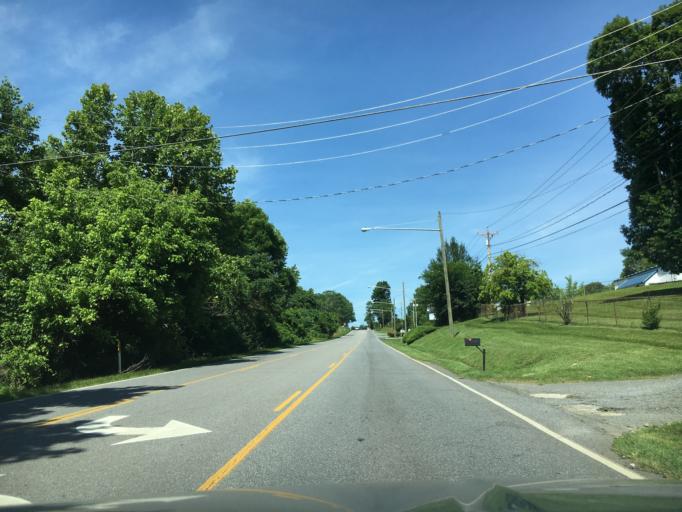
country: US
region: Virginia
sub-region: City of Lynchburg
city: West Lynchburg
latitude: 37.3991
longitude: -79.2114
